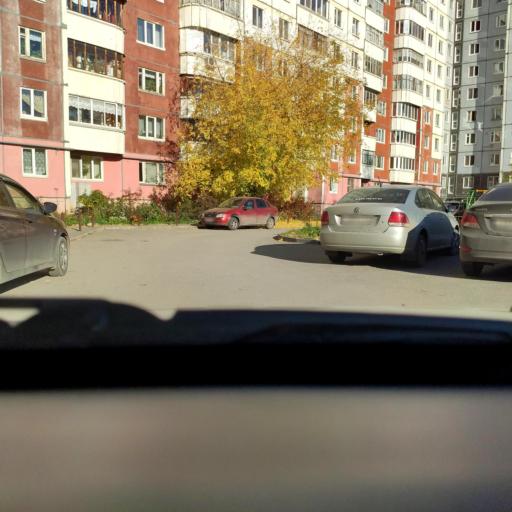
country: RU
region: Perm
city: Perm
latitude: 58.0096
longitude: 56.3102
